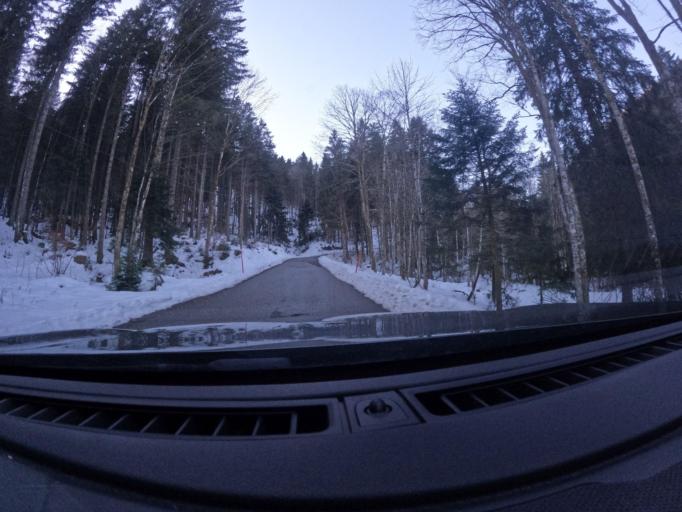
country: DE
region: Bavaria
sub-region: Upper Bavaria
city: Ruhpolding
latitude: 47.7639
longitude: 12.6057
